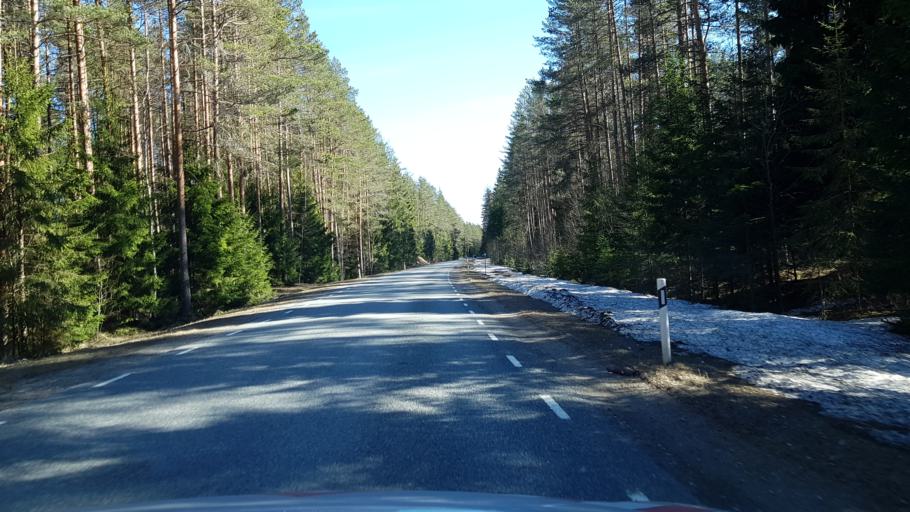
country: EE
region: Laeaene-Virumaa
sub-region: Vinni vald
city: Vinni
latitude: 59.2617
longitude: 26.6805
